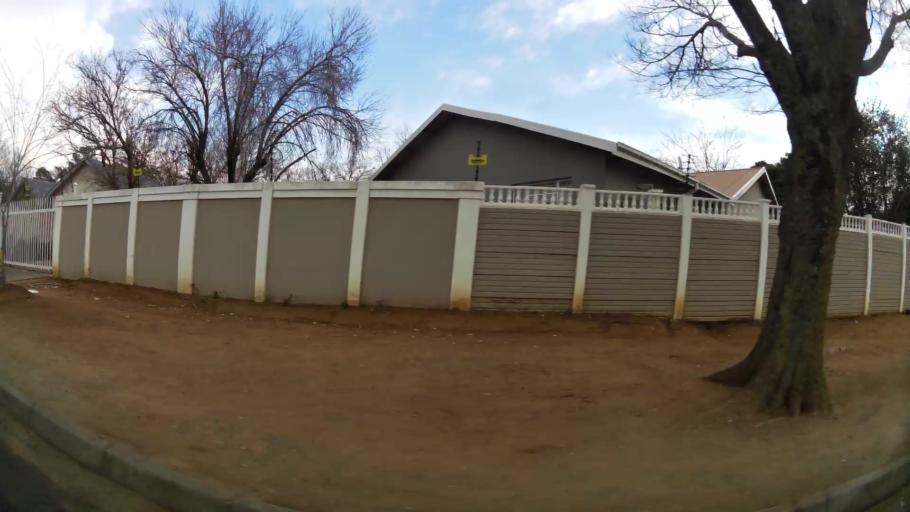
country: ZA
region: Orange Free State
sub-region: Mangaung Metropolitan Municipality
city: Bloemfontein
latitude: -29.1204
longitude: 26.1745
